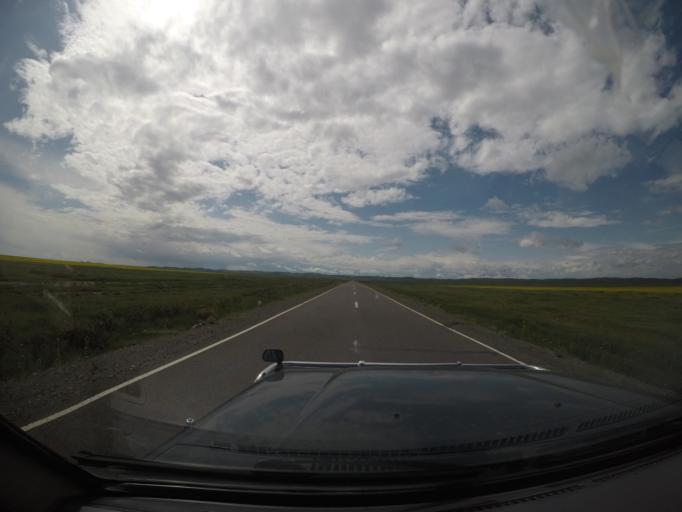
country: MN
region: Hentiy
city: Moron
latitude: 47.4185
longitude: 109.9436
